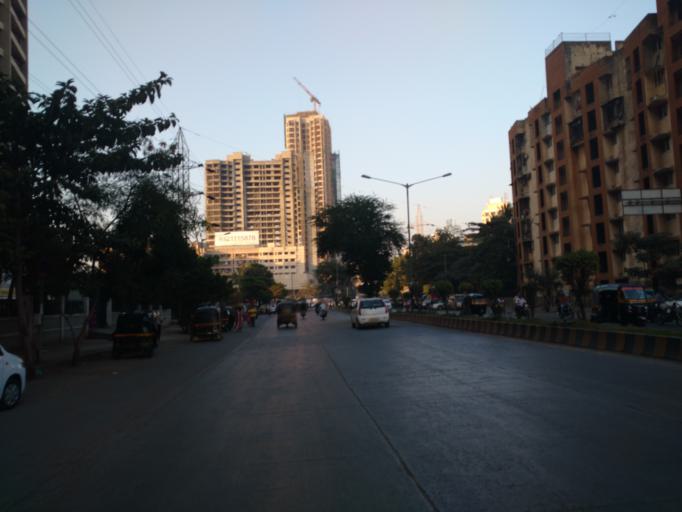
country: IN
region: Maharashtra
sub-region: Mumbai Suburban
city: Borivli
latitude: 19.2092
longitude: 72.8350
